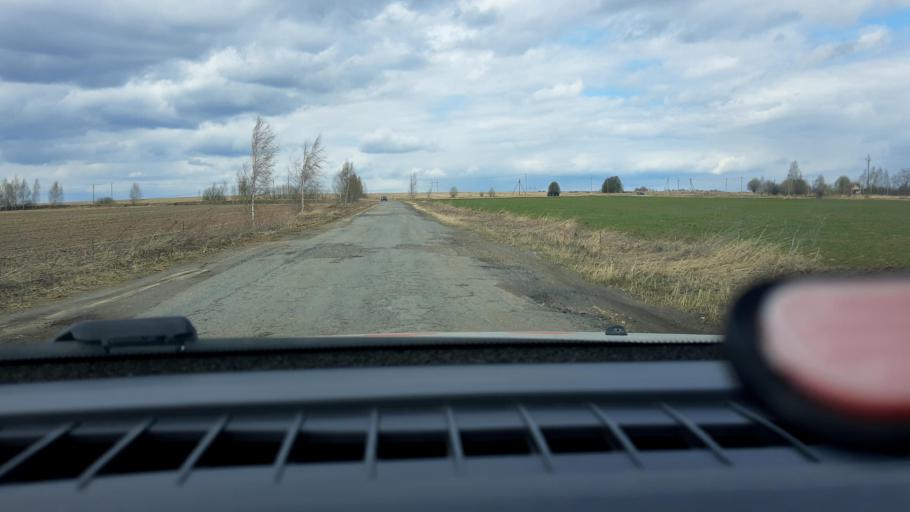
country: RU
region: Nizjnij Novgorod
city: Babino
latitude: 56.1641
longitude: 43.6875
